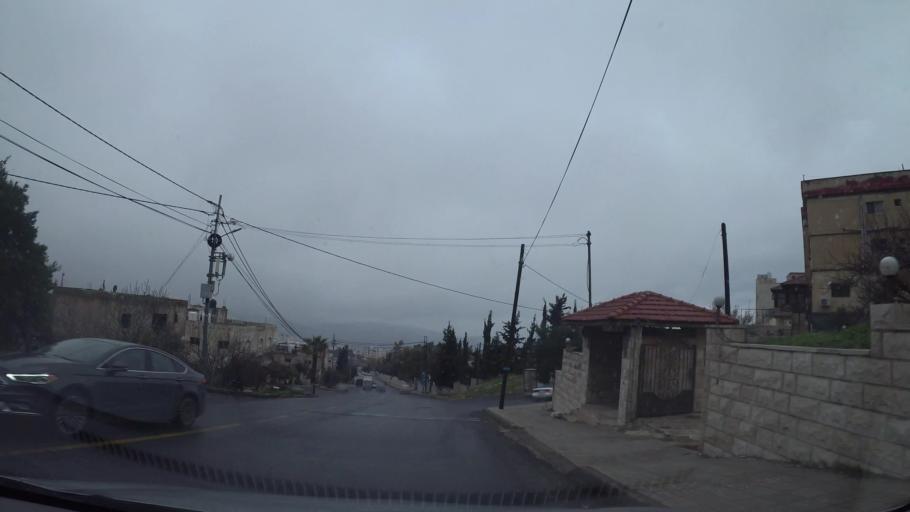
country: JO
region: Amman
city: Al Jubayhah
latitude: 32.0259
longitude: 35.8329
